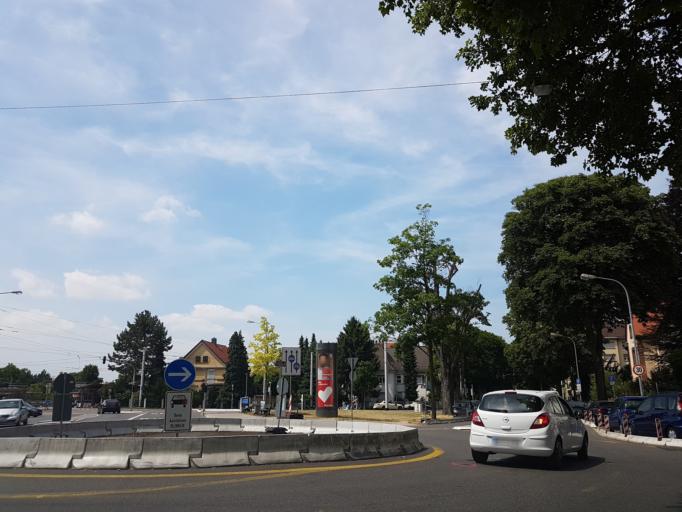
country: DE
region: Baden-Wuerttemberg
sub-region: Karlsruhe Region
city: Heidelberg
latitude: 49.3994
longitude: 8.6901
